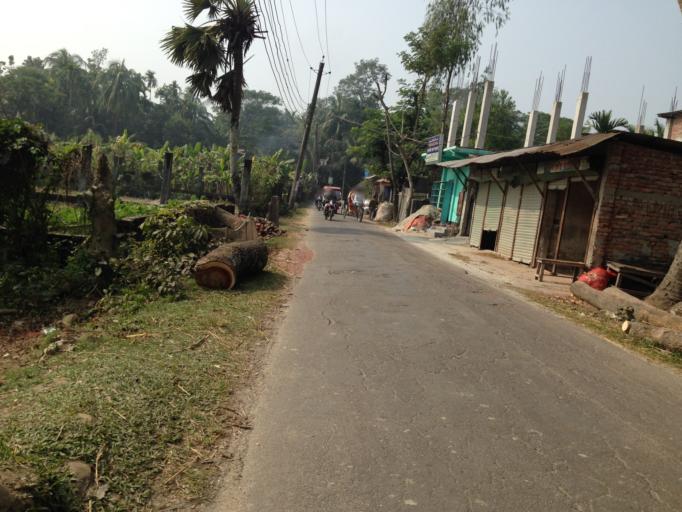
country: BD
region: Chittagong
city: Lakshmipur
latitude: 22.9326
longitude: 90.8184
